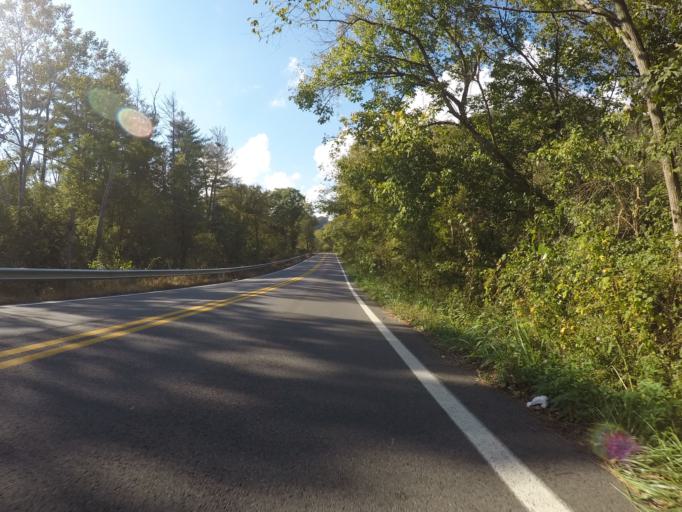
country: US
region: Ohio
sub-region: Lawrence County
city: Burlington
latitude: 38.3728
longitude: -82.5279
